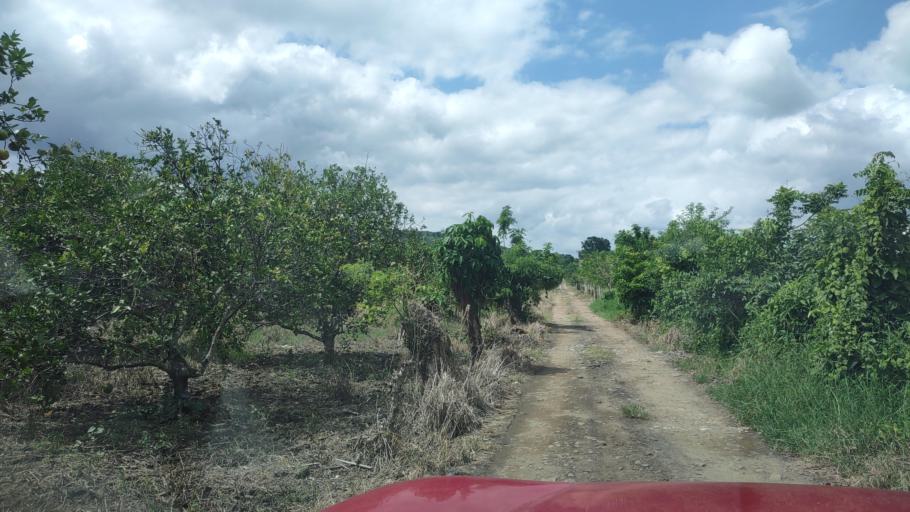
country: MX
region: Puebla
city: San Jose Acateno
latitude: 20.2206
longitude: -97.1449
